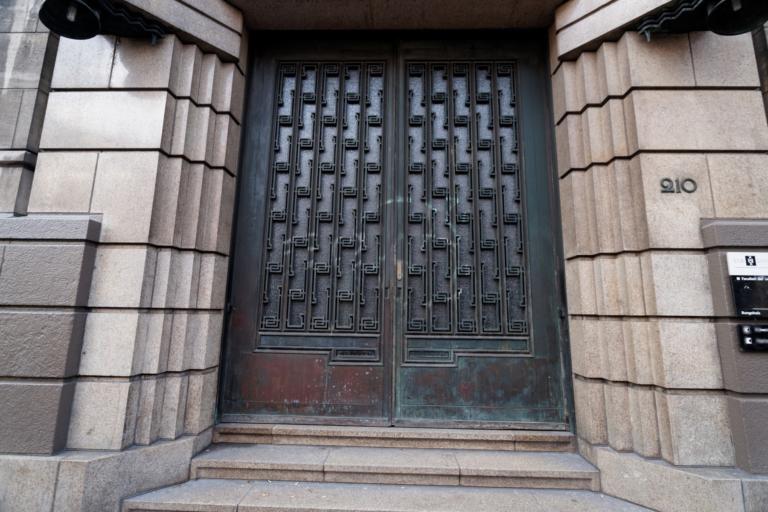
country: NL
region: North Holland
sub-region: Gemeente Amsterdam
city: Amsterdam
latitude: 52.3721
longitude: 4.8893
